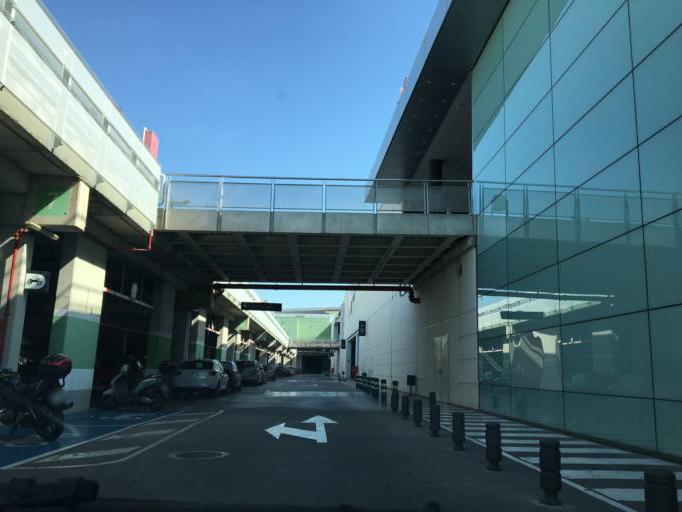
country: ES
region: Murcia
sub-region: Murcia
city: Murcia
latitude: 38.0386
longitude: -1.1494
